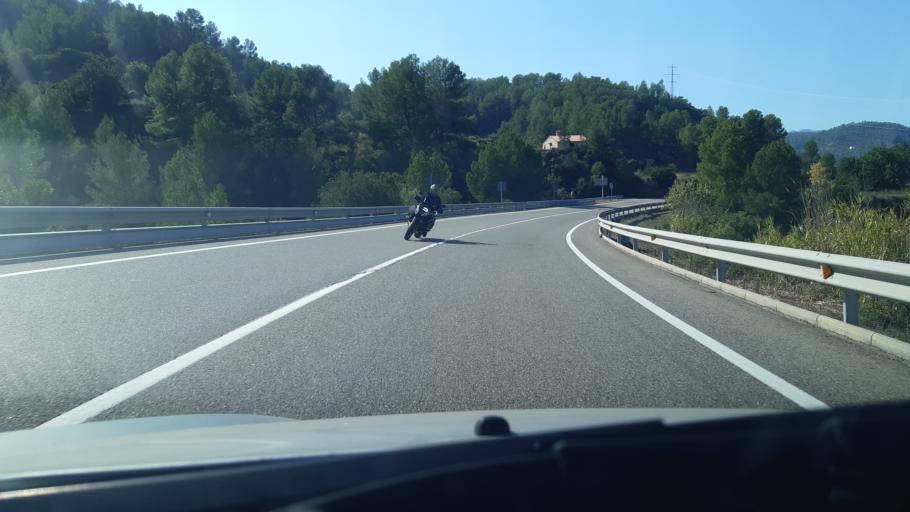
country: ES
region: Catalonia
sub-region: Provincia de Tarragona
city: Benifallet
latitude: 40.9822
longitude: 0.5346
